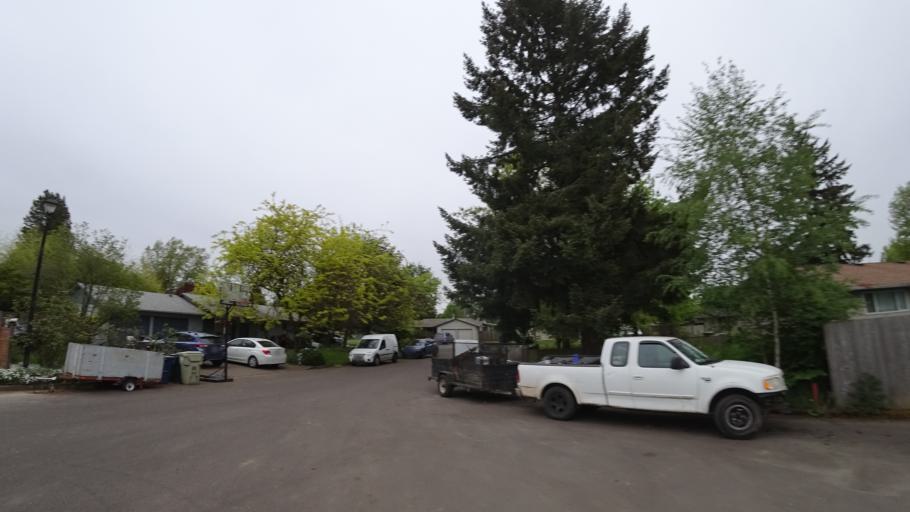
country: US
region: Oregon
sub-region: Washington County
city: Aloha
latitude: 45.5062
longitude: -122.8797
